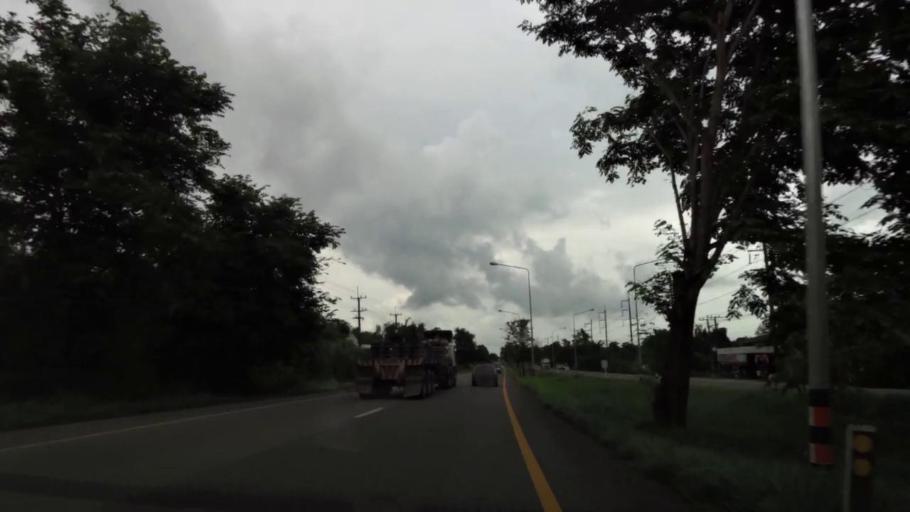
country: TH
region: Chanthaburi
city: Tha Mai
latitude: 12.6954
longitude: 101.9907
